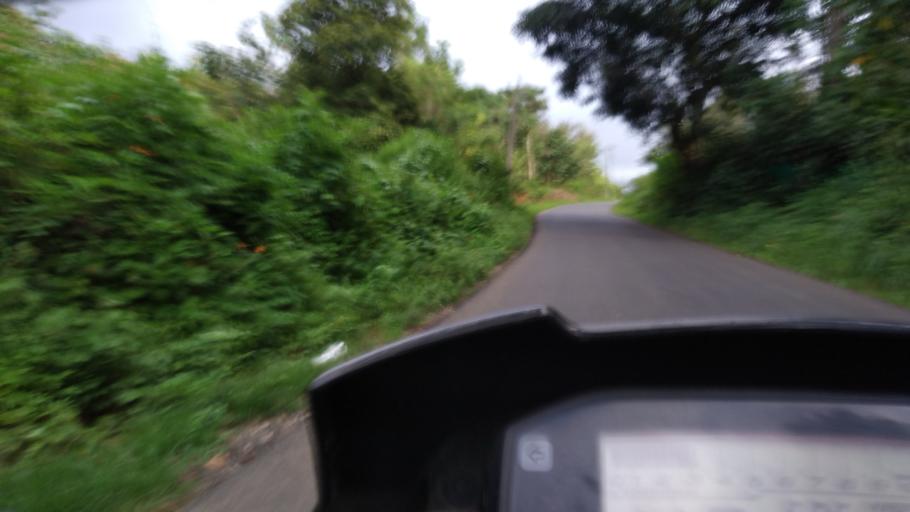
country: IN
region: Tamil Nadu
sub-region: Theni
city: Bodinayakkanur
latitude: 10.0347
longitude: 77.2242
